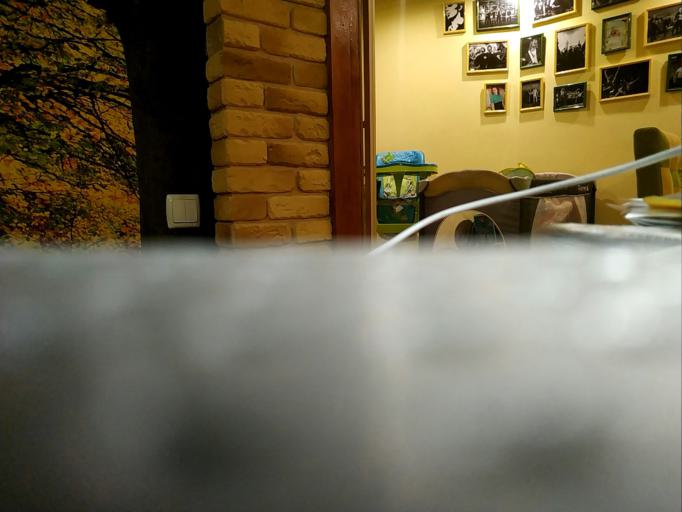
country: RU
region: Tverskaya
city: Spirovo
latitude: 57.3375
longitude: 35.0634
